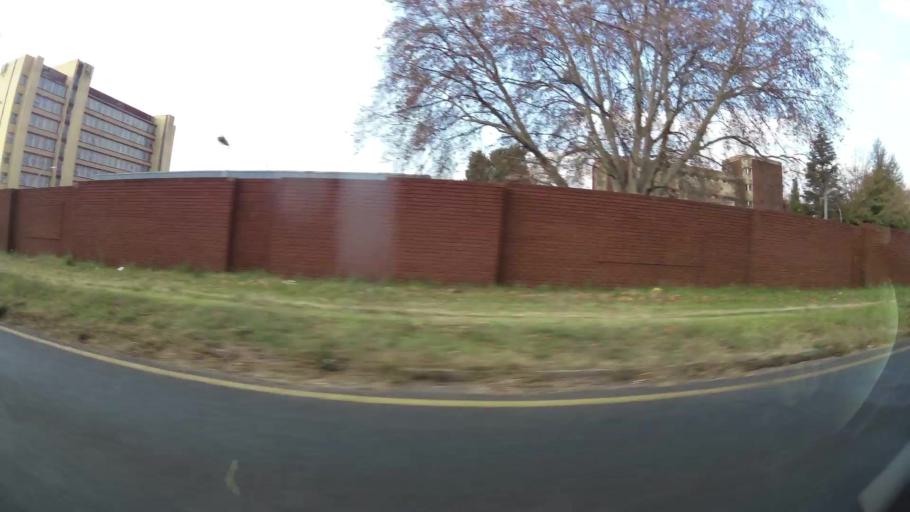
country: ZA
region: Gauteng
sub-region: Ekurhuleni Metropolitan Municipality
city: Benoni
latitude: -26.1589
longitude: 28.3047
